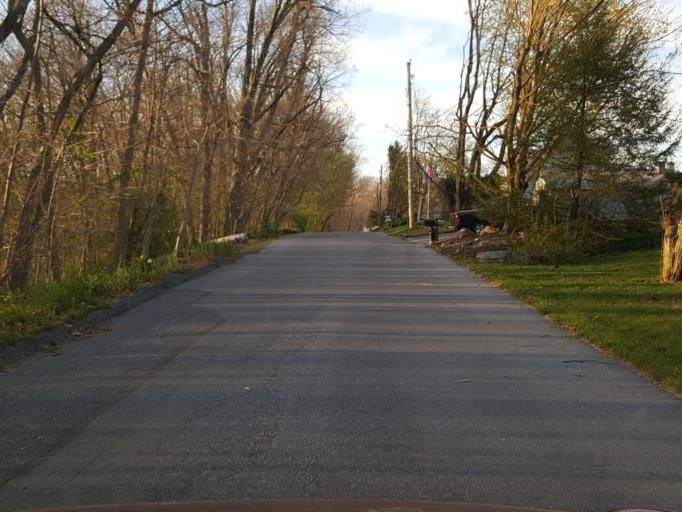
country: US
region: Pennsylvania
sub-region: Dauphin County
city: Hummelstown
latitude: 40.2403
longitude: -76.7264
